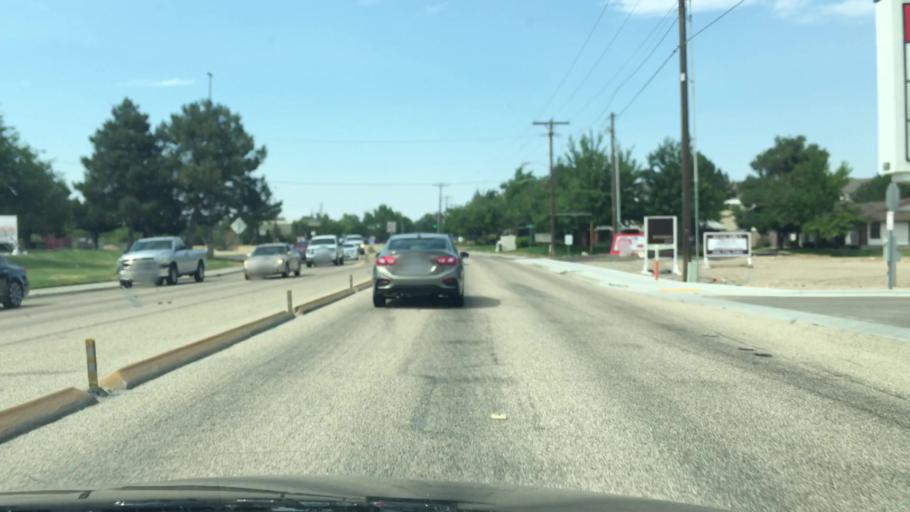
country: US
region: Idaho
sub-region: Ada County
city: Garden City
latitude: 43.6096
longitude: -116.2739
